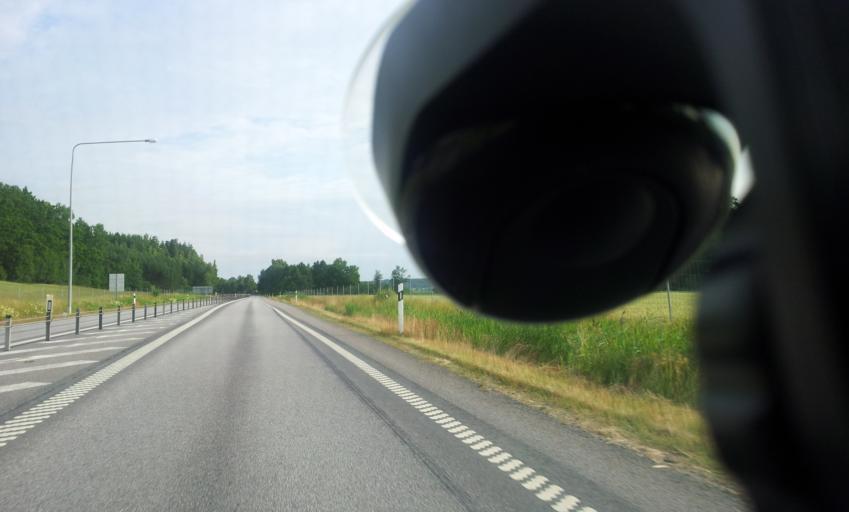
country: SE
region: OEstergoetland
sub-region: Valdemarsviks Kommun
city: Gusum
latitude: 58.3186
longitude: 16.4791
